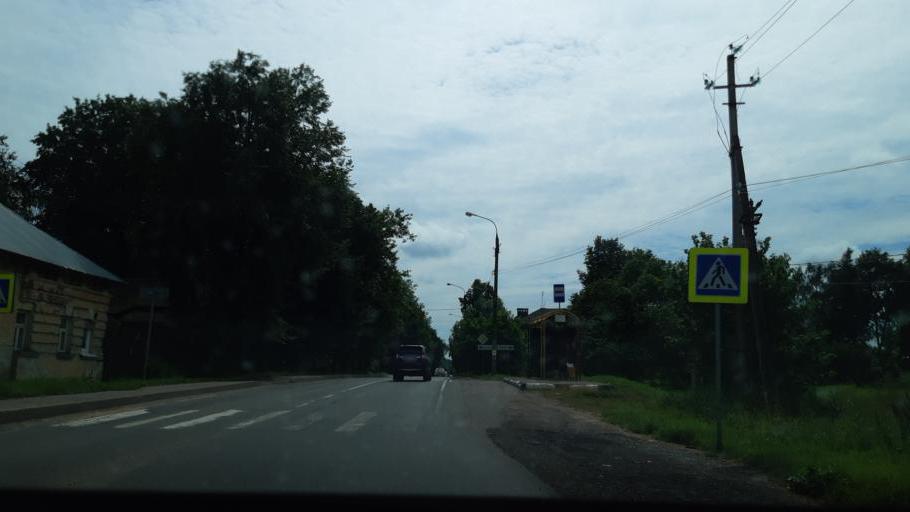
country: RU
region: Moskovskaya
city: Vereya
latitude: 55.3446
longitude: 36.1768
